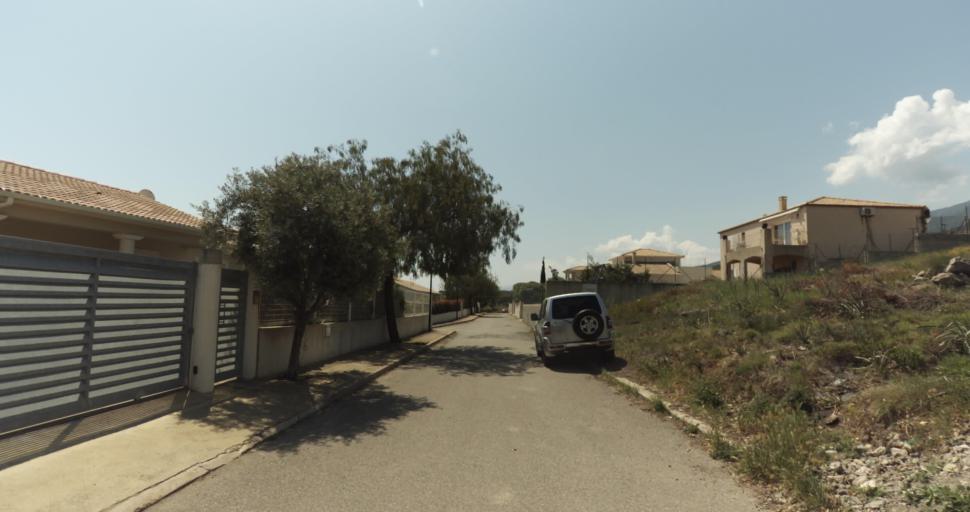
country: FR
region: Corsica
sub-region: Departement de la Haute-Corse
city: Biguglia
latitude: 42.6009
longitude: 9.4306
